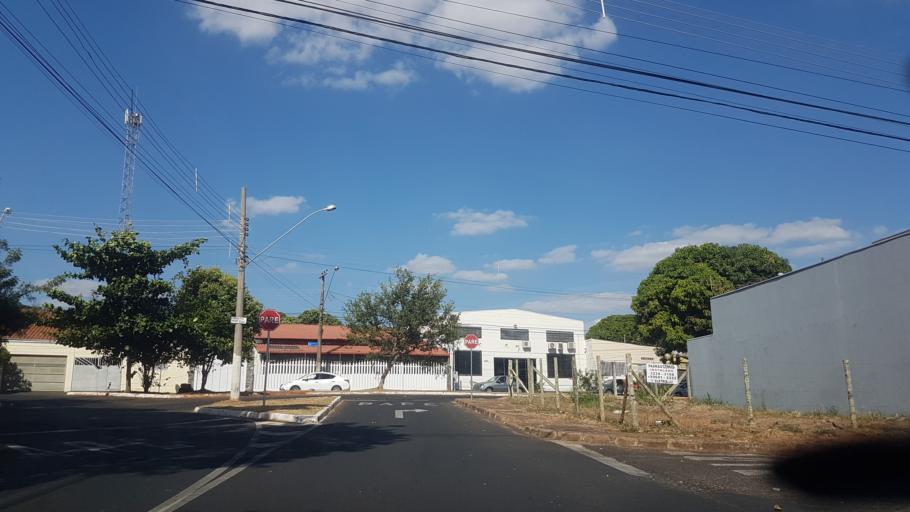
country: BR
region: Minas Gerais
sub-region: Uberlandia
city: Uberlandia
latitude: -18.9005
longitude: -48.2572
